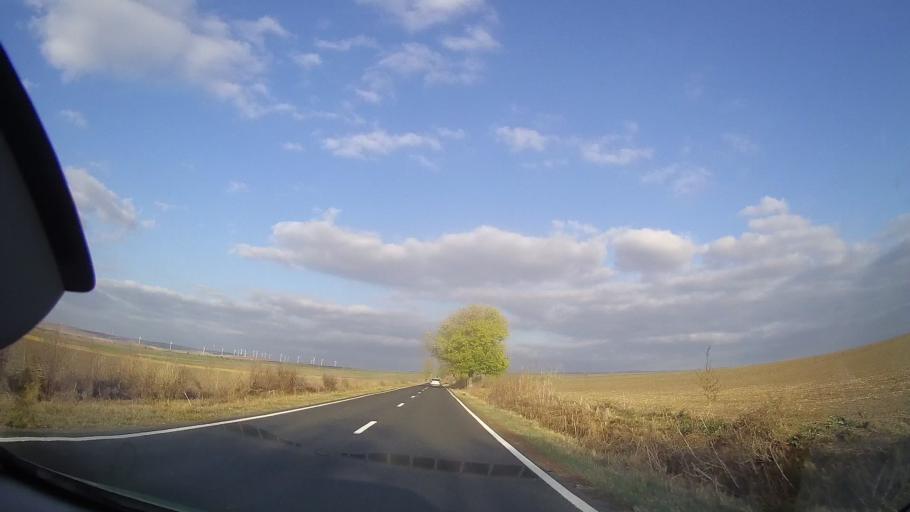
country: RO
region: Tulcea
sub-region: Comuna Topolog
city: Topolog
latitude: 44.8380
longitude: 28.2990
